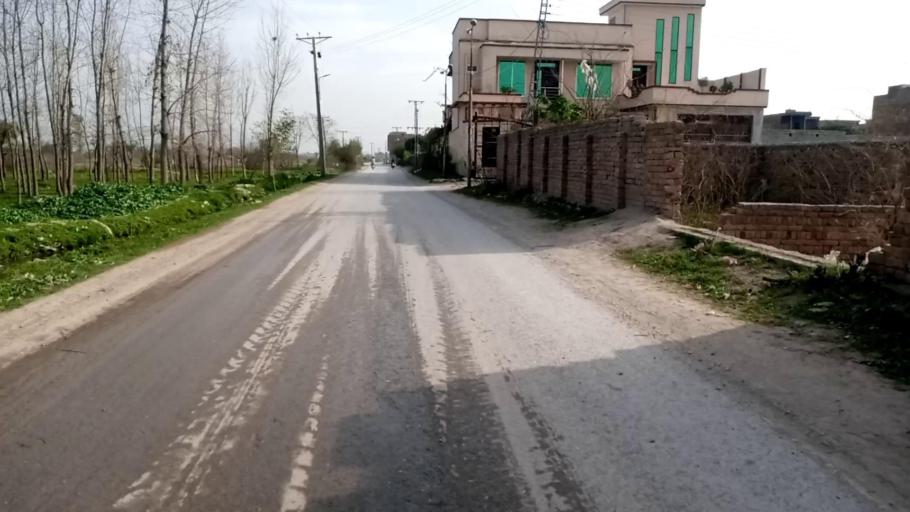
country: PK
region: Khyber Pakhtunkhwa
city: Peshawar
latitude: 34.0107
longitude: 71.4471
